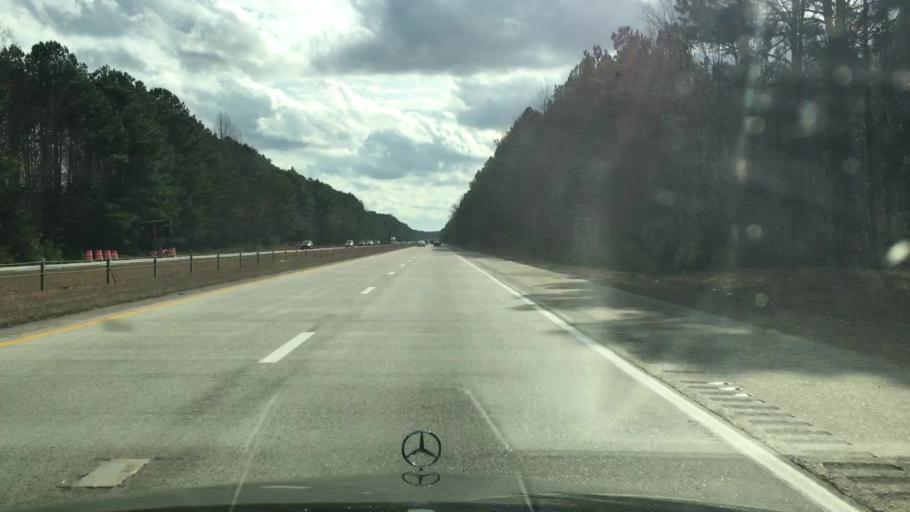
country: US
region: North Carolina
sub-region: Johnston County
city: Benson
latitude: 35.5041
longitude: -78.5549
